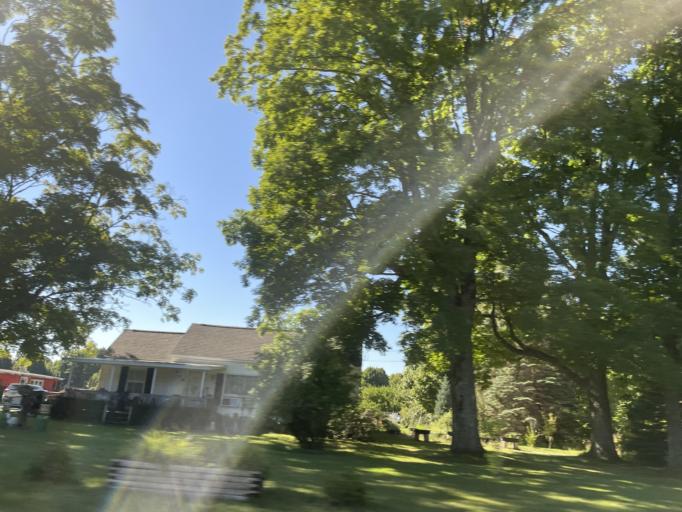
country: US
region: Michigan
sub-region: Benzie County
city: Beulah
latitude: 44.6173
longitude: -86.0564
